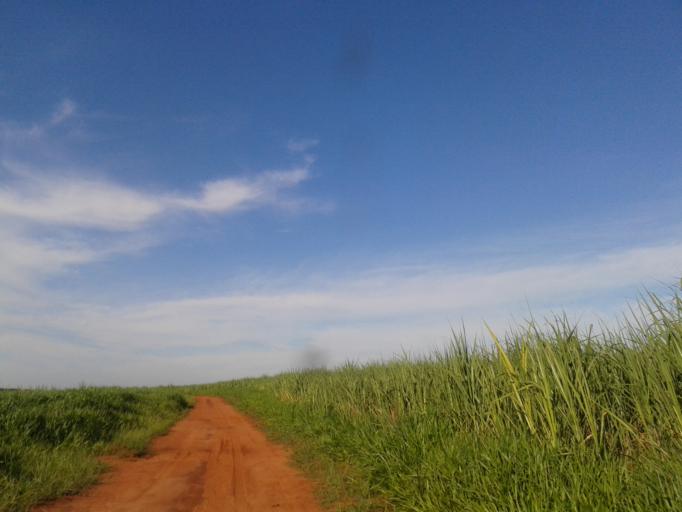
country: BR
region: Minas Gerais
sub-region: Santa Vitoria
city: Santa Vitoria
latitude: -19.0944
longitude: -49.9864
